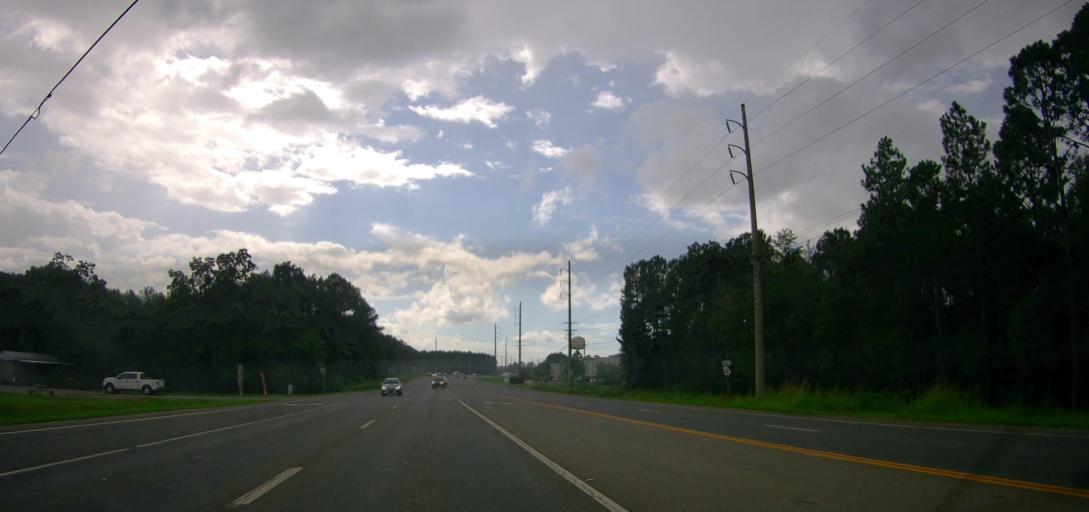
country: US
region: Georgia
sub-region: Coffee County
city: Douglas
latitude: 31.4881
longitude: -82.8601
